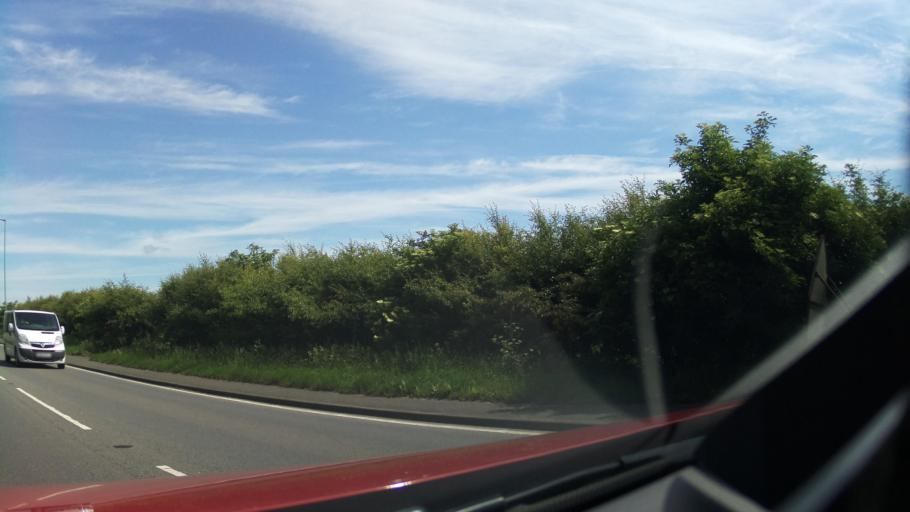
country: GB
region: England
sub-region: Lincolnshire
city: Burton
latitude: 53.2943
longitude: -0.5410
